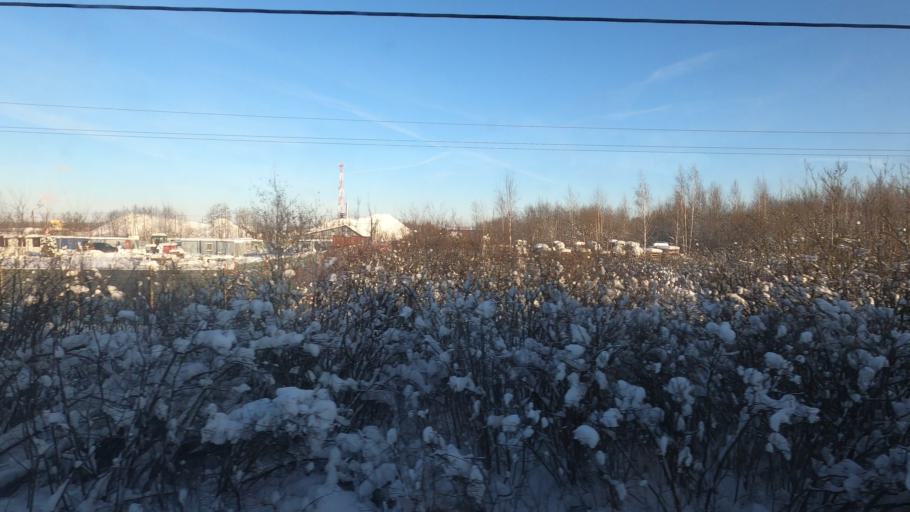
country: RU
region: Moskovskaya
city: Taldom
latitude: 56.7129
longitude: 37.5394
